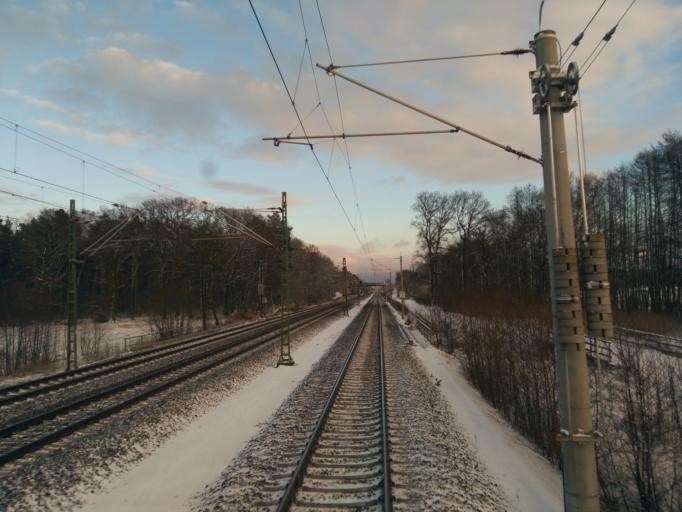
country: DE
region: Lower Saxony
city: Radbruch
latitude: 53.3151
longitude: 10.2976
